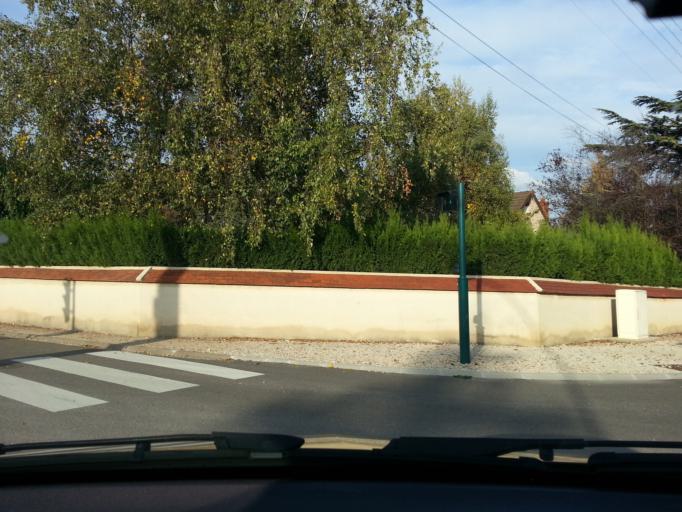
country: FR
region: Bourgogne
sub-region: Departement de Saone-et-Loire
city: Saint-Remy
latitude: 46.7739
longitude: 4.8210
